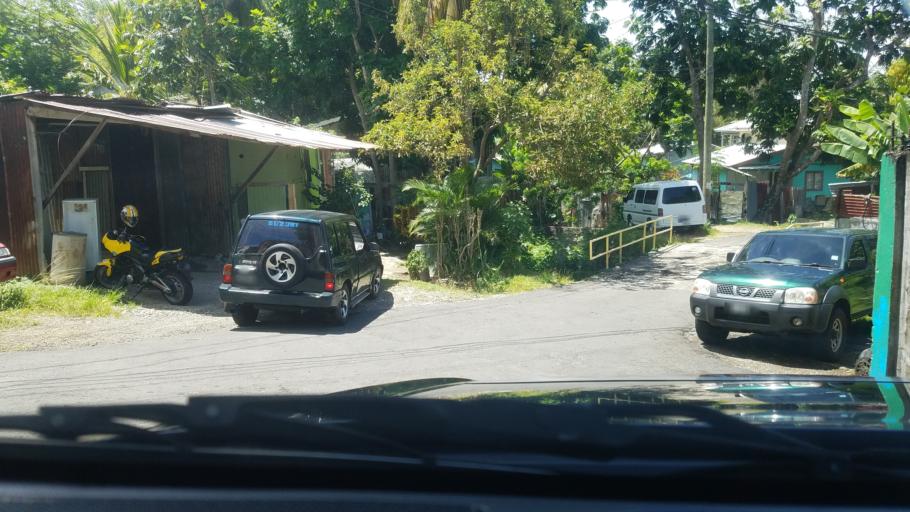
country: LC
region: Castries Quarter
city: Castries
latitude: 14.0037
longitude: -60.9877
